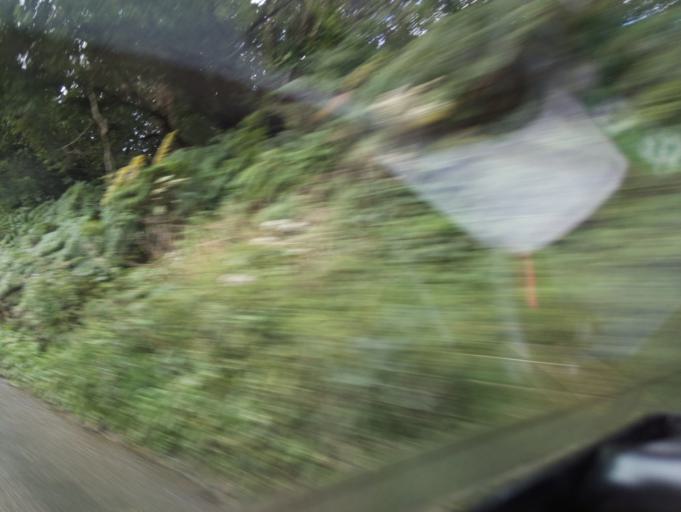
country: GB
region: England
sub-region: Devon
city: Modbury
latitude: 50.3341
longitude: -3.8509
